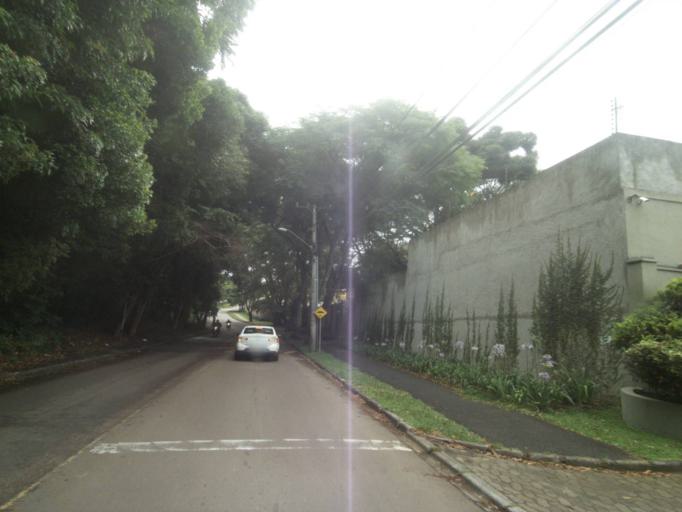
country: BR
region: Parana
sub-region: Curitiba
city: Curitiba
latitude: -25.4523
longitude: -49.3286
